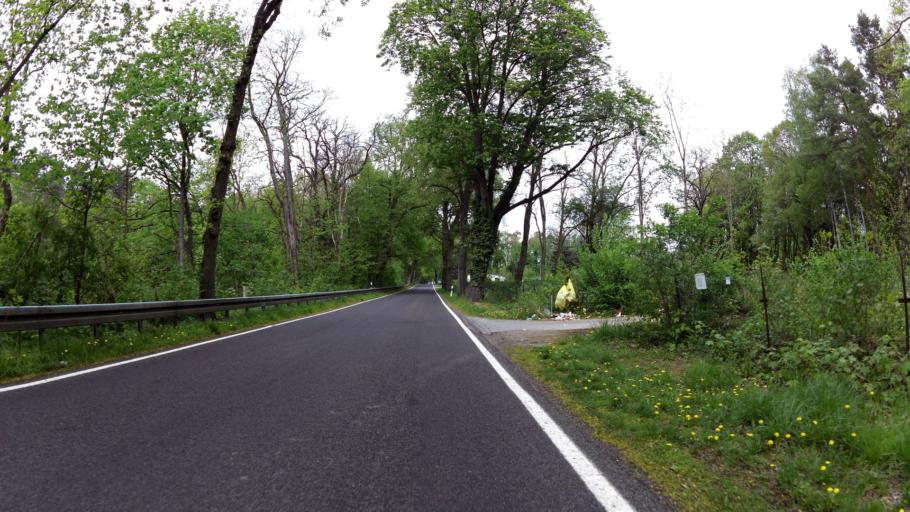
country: DE
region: Brandenburg
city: Mittenwalde
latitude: 52.1982
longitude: 13.5760
